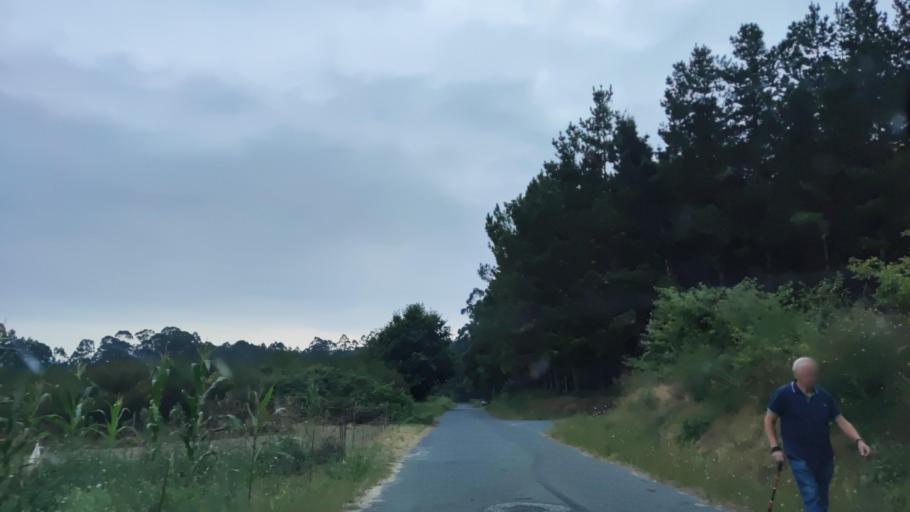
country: ES
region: Galicia
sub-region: Provincia de Pontevedra
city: Catoira
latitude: 42.6947
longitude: -8.7307
